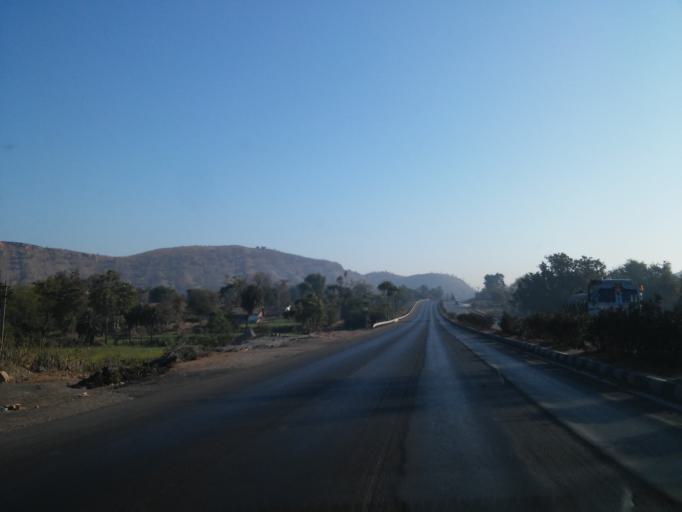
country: IN
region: Rajasthan
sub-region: Dungarpur
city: Dungarpur
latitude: 23.9998
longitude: 73.6419
